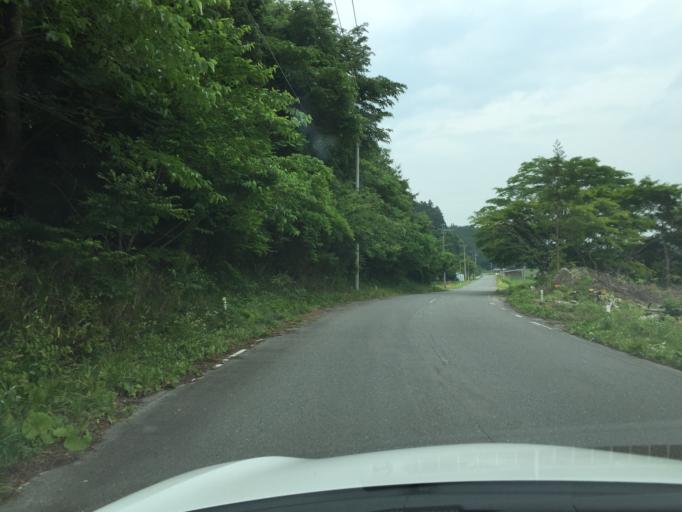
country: JP
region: Fukushima
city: Iwaki
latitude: 37.1750
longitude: 140.7134
